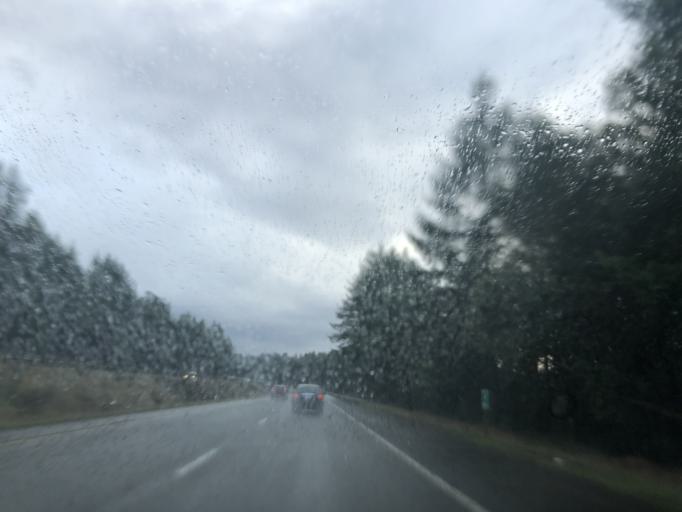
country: US
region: Washington
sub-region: Pierce County
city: Purdy
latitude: 47.3748
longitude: -122.6176
